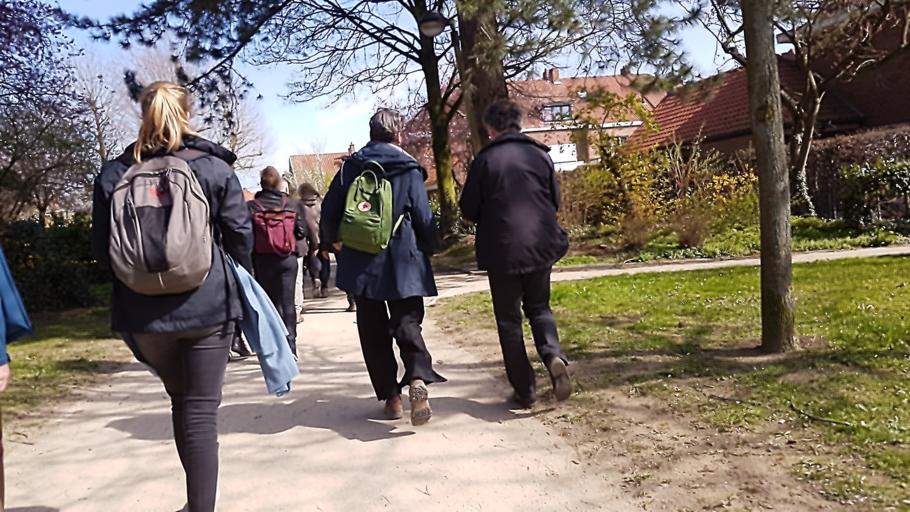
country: BE
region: Flanders
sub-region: Provincie West-Vlaanderen
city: Kortrijk
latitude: 50.8156
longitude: 3.2771
